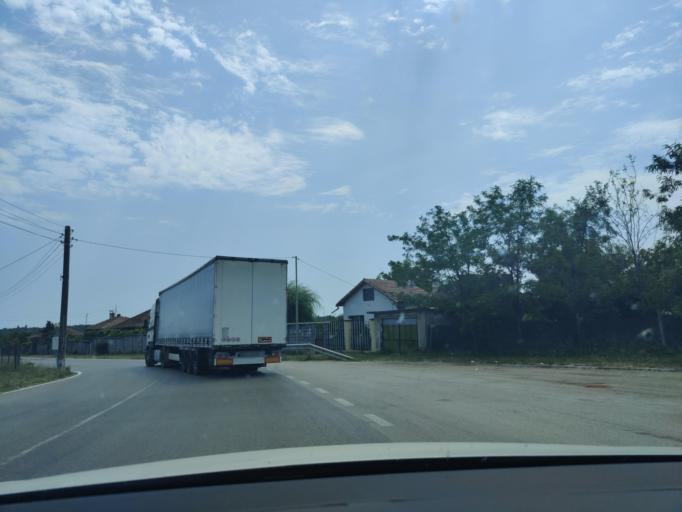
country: BG
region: Vidin
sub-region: Obshtina Ruzhintsi
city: Ruzhintsi
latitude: 43.6552
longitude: 22.7785
